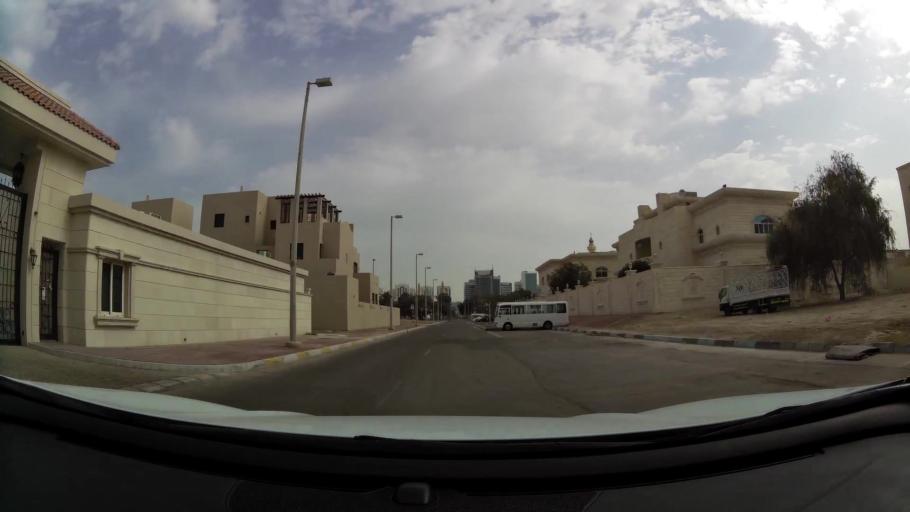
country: AE
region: Abu Dhabi
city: Abu Dhabi
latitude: 24.4555
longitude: 54.3730
